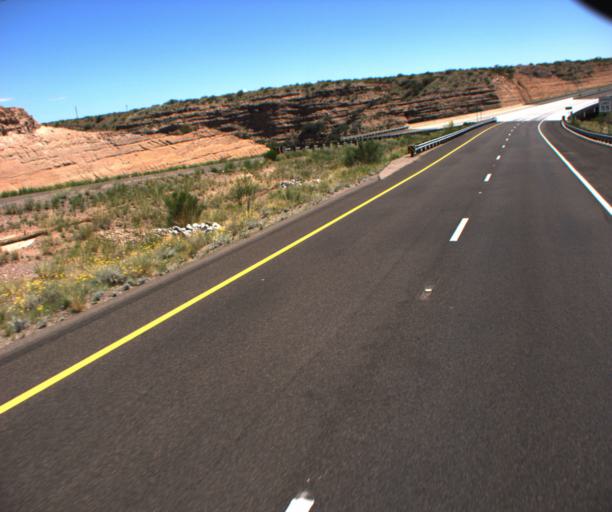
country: US
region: Arizona
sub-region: Greenlee County
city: Clifton
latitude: 32.9558
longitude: -109.2307
